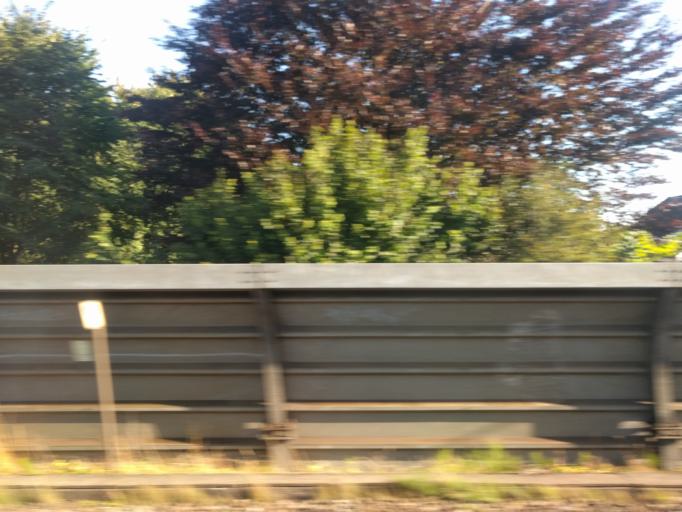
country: DK
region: Zealand
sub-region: Ringsted Kommune
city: Ringsted
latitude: 55.4373
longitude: 11.7694
